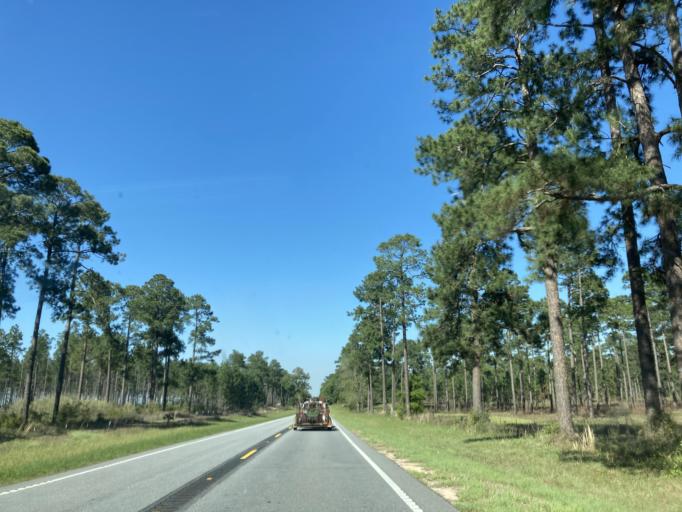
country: US
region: Georgia
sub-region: Baker County
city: Newton
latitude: 31.3566
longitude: -84.2977
